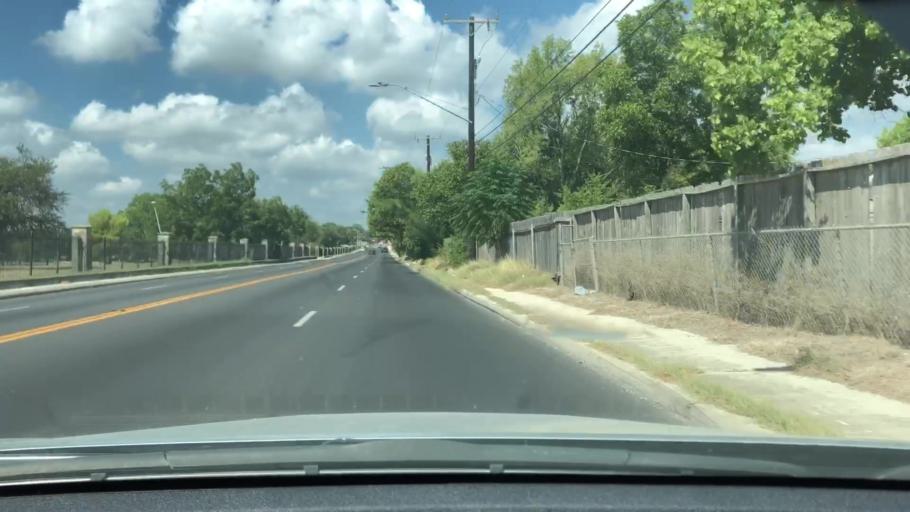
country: US
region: Texas
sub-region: Bexar County
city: Terrell Hills
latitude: 29.4849
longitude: -98.4240
